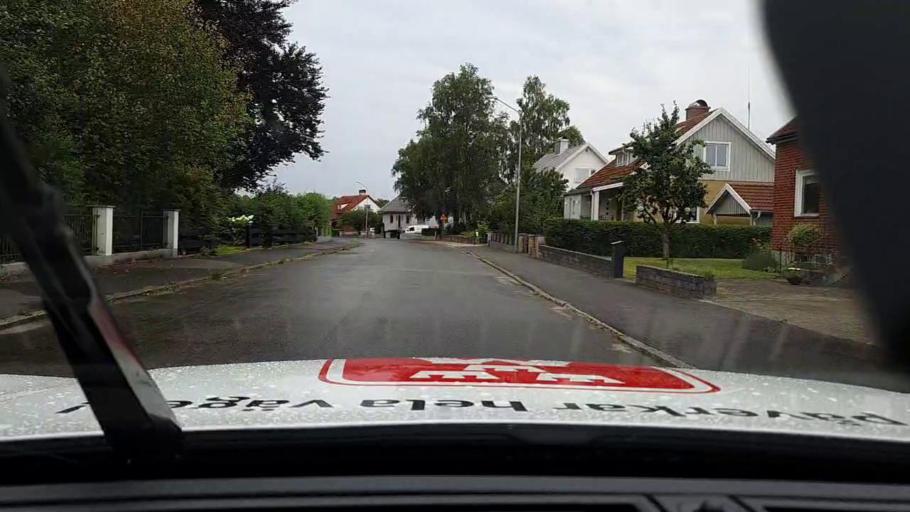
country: SE
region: Skane
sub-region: Hassleholms Kommun
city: Hassleholm
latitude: 56.1664
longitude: 13.7741
